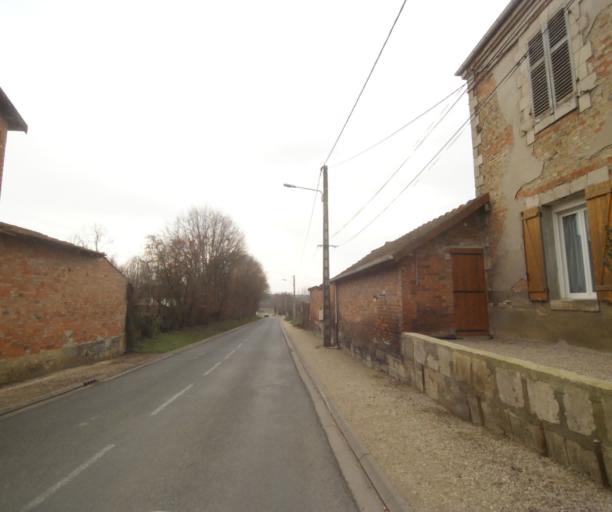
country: FR
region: Champagne-Ardenne
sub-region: Departement de la Marne
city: Pargny-sur-Saulx
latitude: 48.7484
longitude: 4.8479
